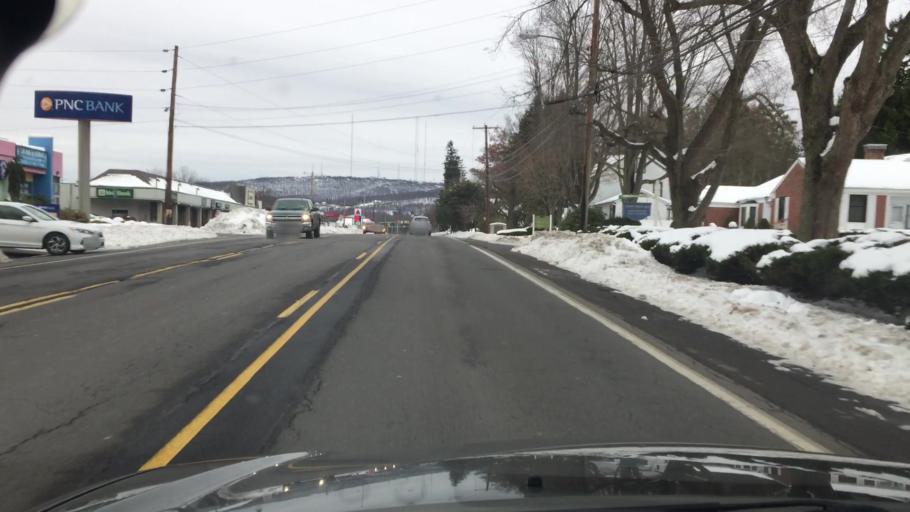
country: US
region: Pennsylvania
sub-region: Luzerne County
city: Mountain Top
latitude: 41.1548
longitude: -75.8920
